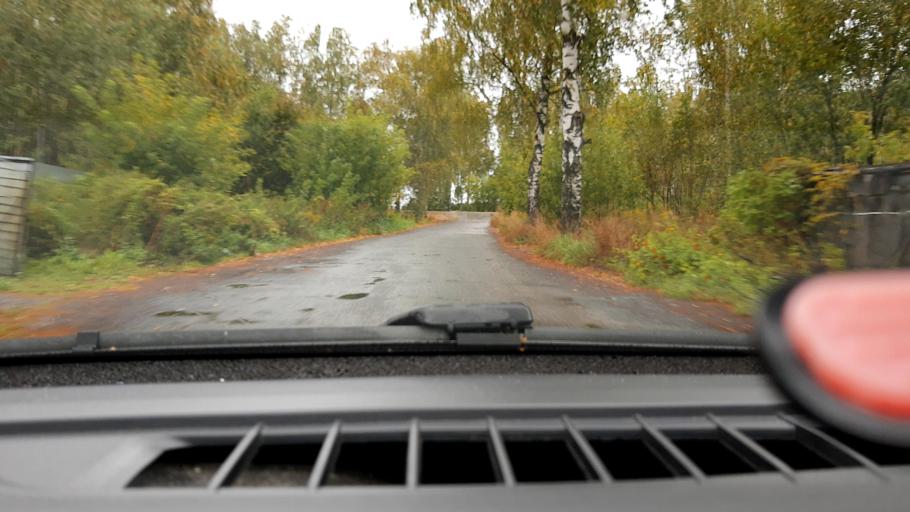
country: RU
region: Nizjnij Novgorod
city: Afonino
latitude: 56.1882
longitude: 44.1187
